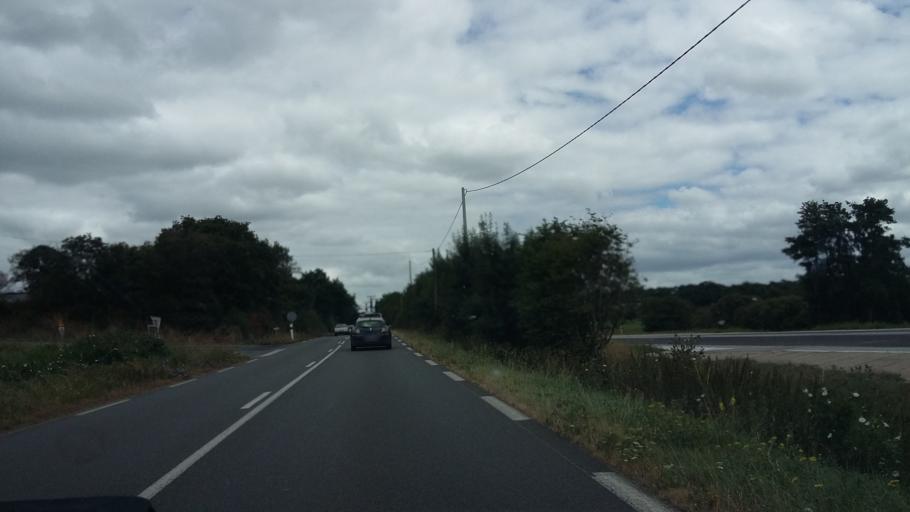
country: FR
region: Pays de la Loire
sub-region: Departement de la Vendee
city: Saint-Christophe-du-Ligneron
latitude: 46.8270
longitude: -1.7934
